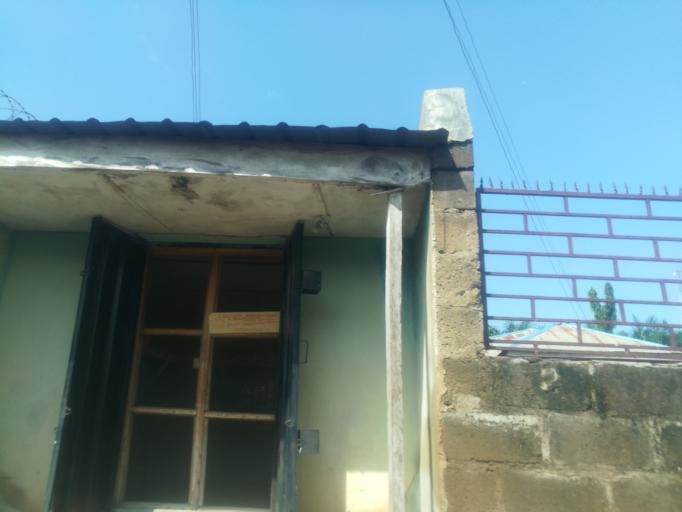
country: NG
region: Oyo
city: Egbeda
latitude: 7.4171
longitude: 3.9784
